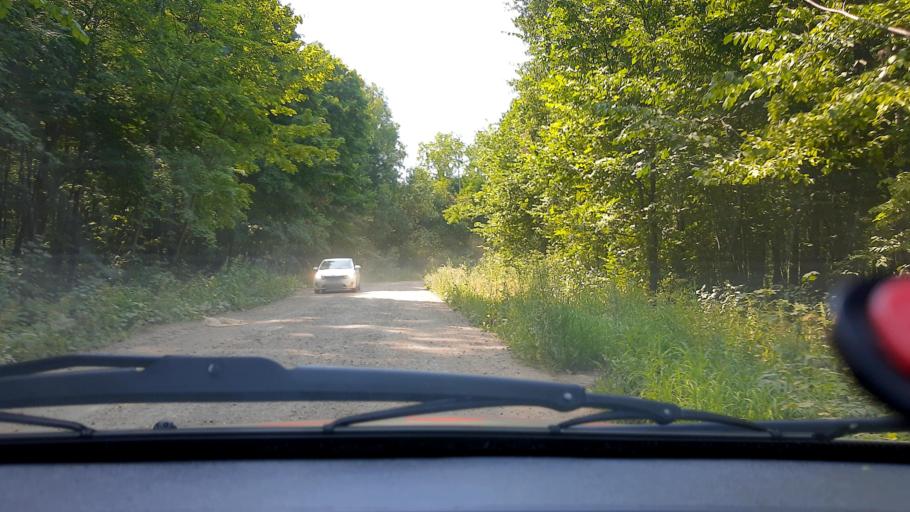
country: RU
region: Bashkortostan
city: Karmaskaly
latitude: 54.3862
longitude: 55.8933
